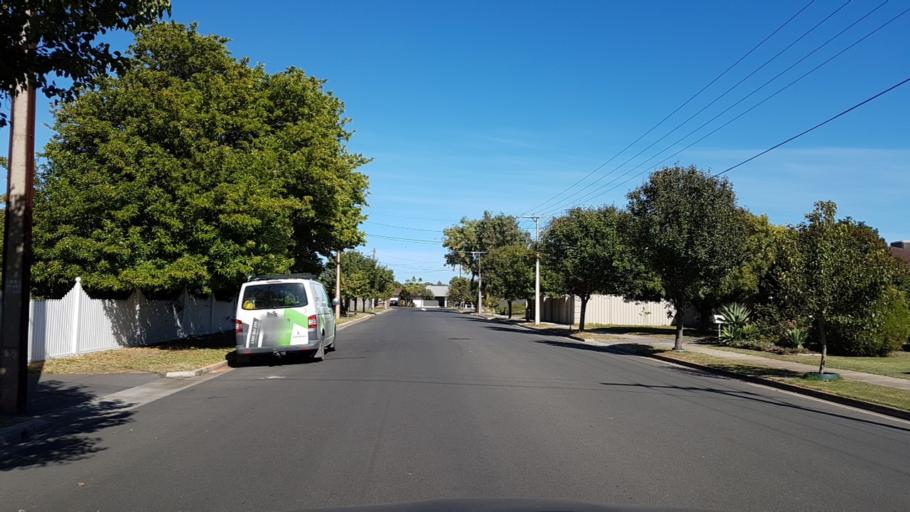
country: AU
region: South Australia
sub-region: Charles Sturt
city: Henley Beach
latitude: -34.9397
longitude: 138.5099
